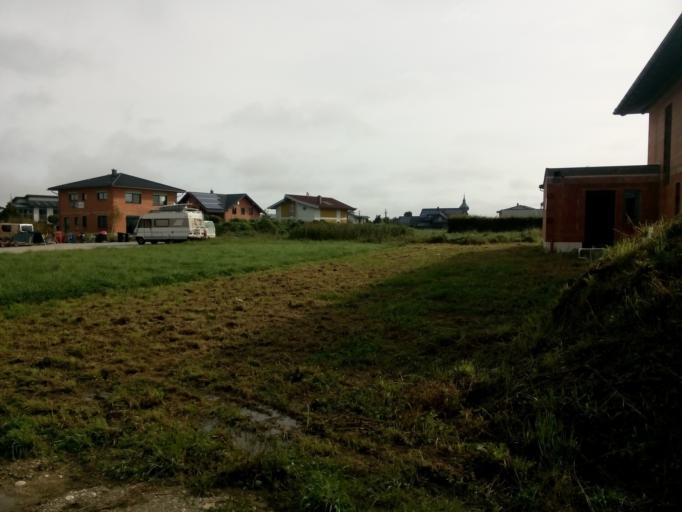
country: AT
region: Upper Austria
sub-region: Politischer Bezirk Gmunden
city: Vorchdorf
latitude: 48.0428
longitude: 13.9749
